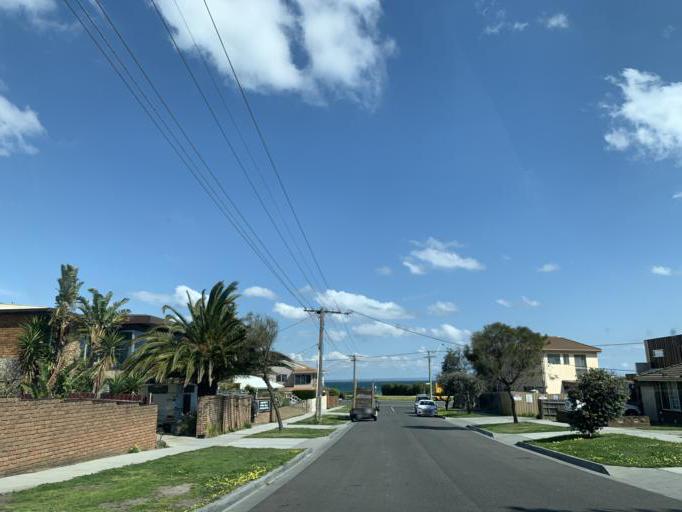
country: AU
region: Victoria
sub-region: Kingston
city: Mordialloc
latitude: -38.0027
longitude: 145.0802
